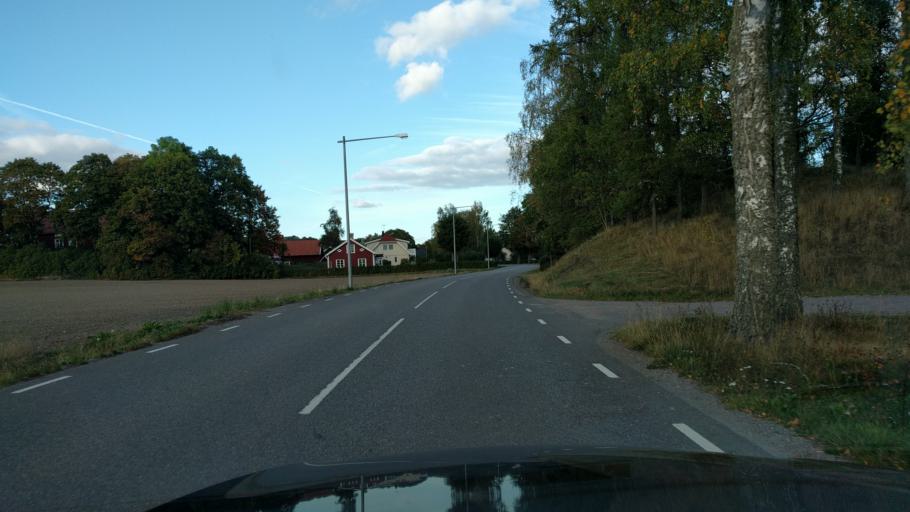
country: SE
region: Uppsala
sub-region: Tierps Kommun
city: Orbyhus
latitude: 60.1576
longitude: 17.5963
